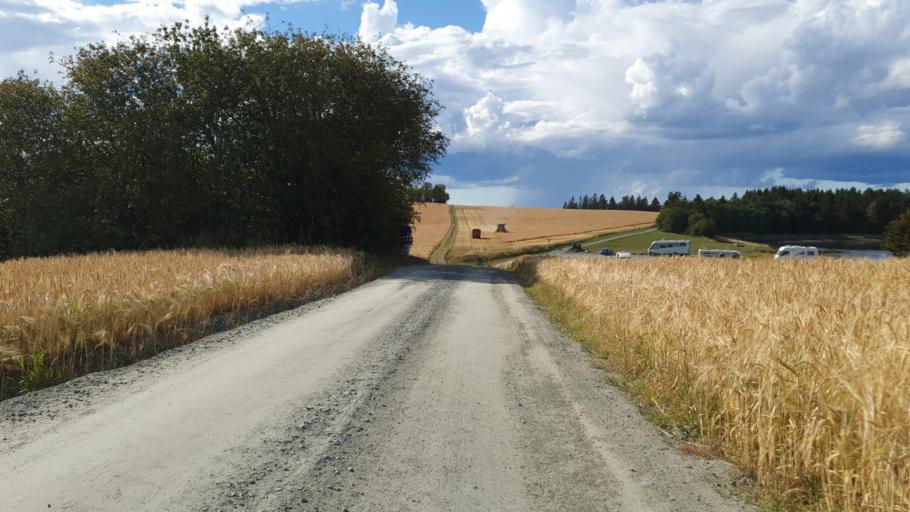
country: NO
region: Nord-Trondelag
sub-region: Verdal
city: Verdal
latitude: 63.7773
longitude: 11.3943
